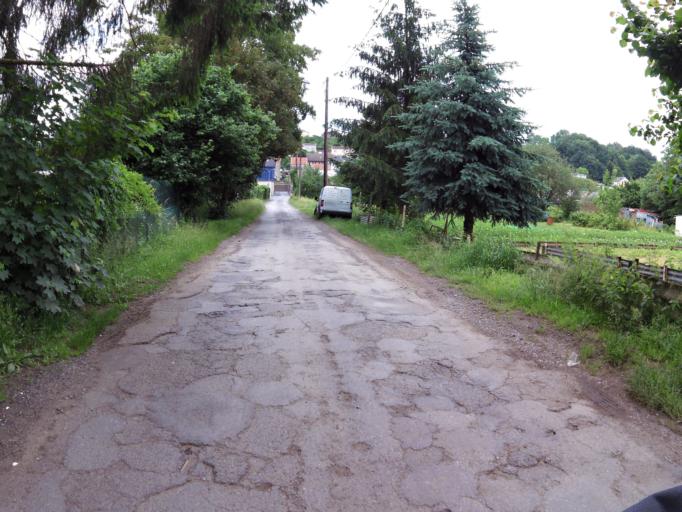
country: FR
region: Champagne-Ardenne
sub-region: Departement des Ardennes
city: Villers-Semeuse
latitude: 49.7569
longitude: 4.7390
